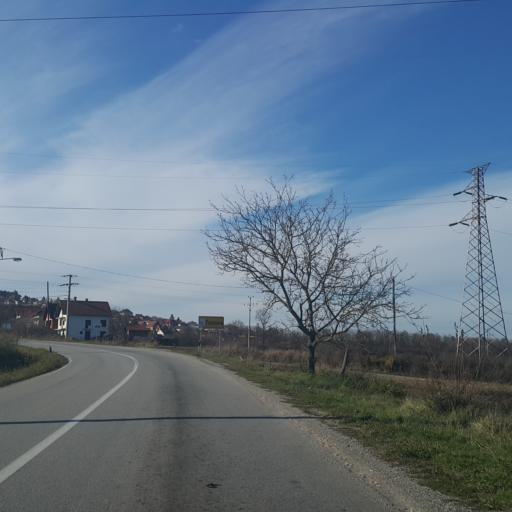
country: RS
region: Central Serbia
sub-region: Sumadijski Okrug
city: Topola
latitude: 44.2494
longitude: 20.6991
